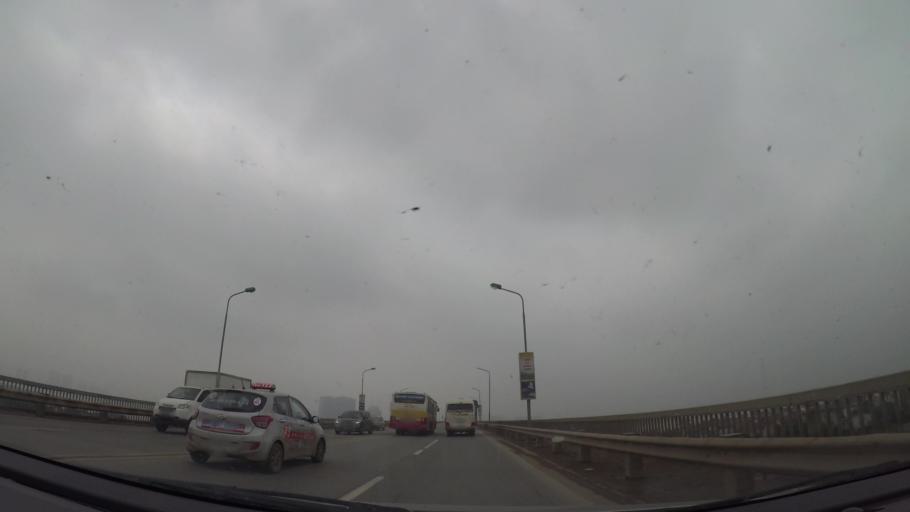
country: VN
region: Ha Noi
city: Tay Ho
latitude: 21.1044
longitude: 105.7868
